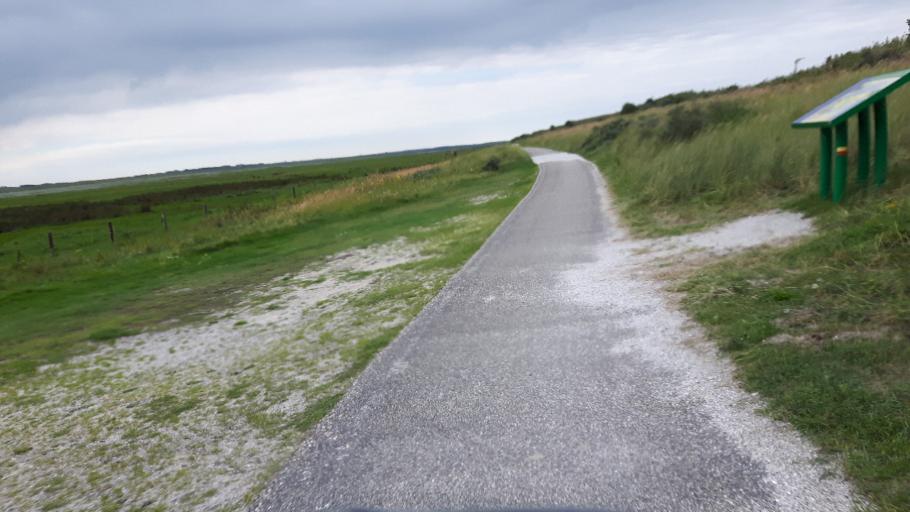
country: NL
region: Friesland
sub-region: Gemeente Dongeradeel
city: Holwerd
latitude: 53.4602
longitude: 5.8862
